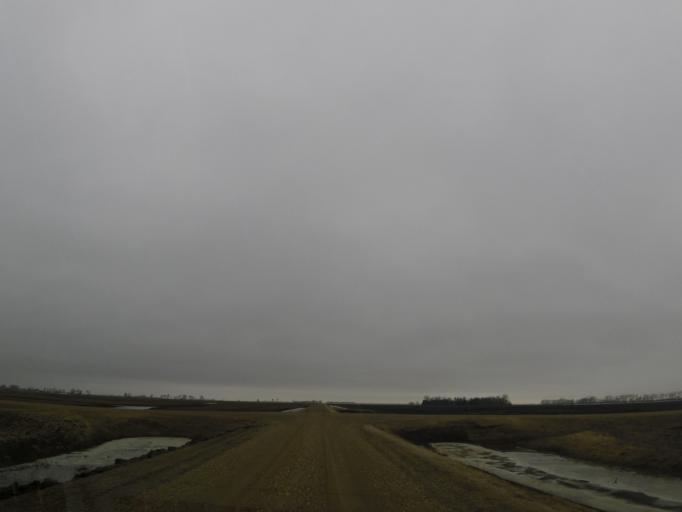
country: US
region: North Dakota
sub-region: Walsh County
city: Grafton
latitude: 48.3831
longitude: -97.2112
